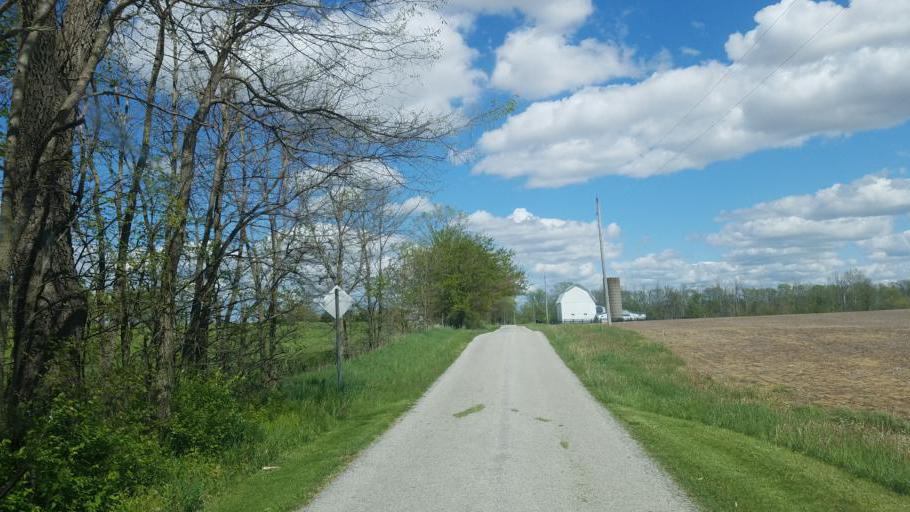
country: US
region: Ohio
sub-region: Marion County
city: Prospect
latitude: 40.4283
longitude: -83.1840
